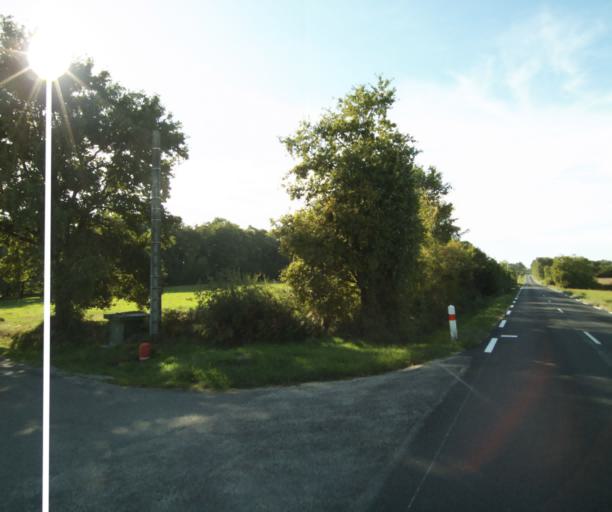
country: FR
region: Midi-Pyrenees
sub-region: Departement du Gers
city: Eauze
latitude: 43.8685
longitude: 0.0492
